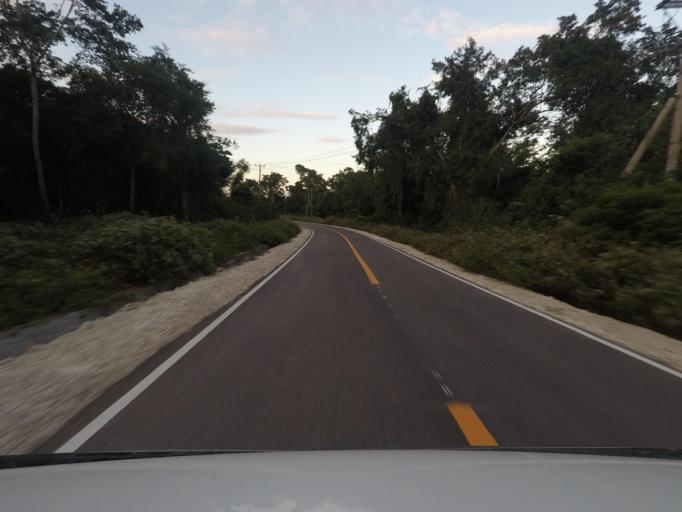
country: TL
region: Lautem
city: Lospalos
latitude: -8.4030
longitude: 127.2871
